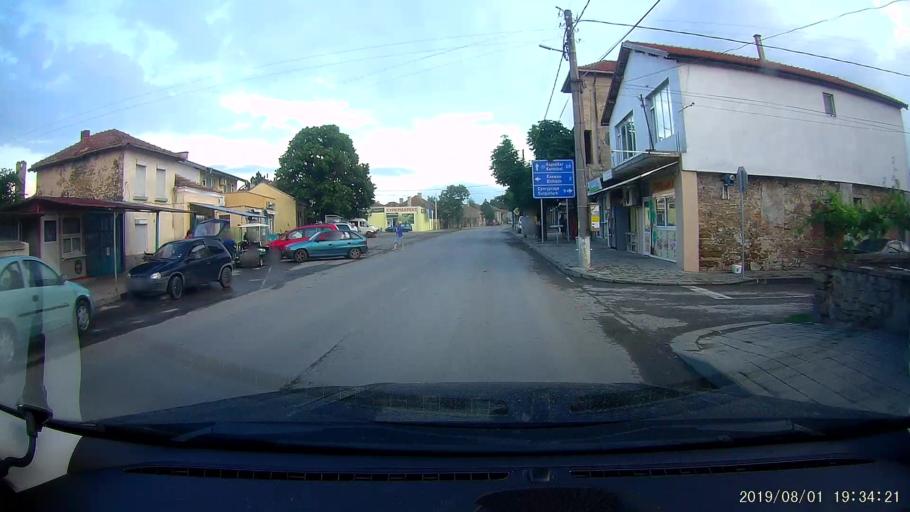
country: BG
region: Burgas
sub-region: Obshtina Sungurlare
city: Sungurlare
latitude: 42.7716
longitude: 26.8781
